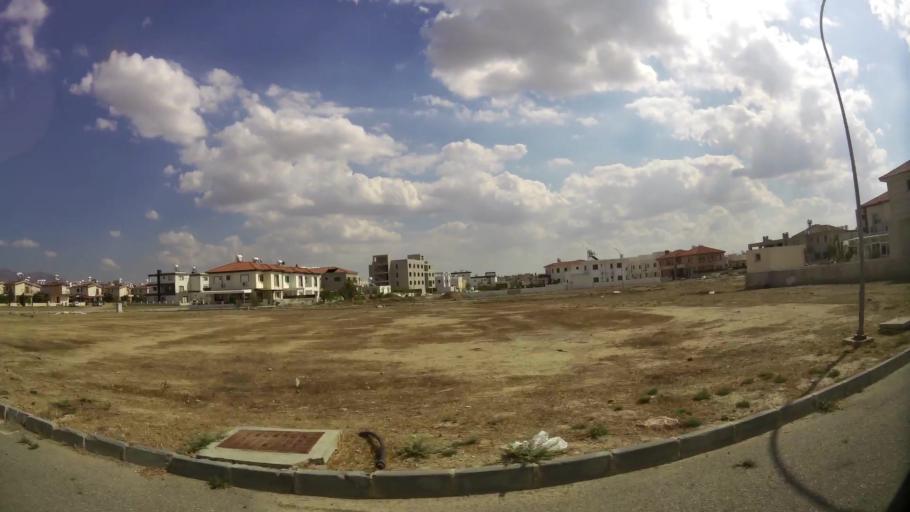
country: CY
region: Lefkosia
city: Nicosia
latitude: 35.2206
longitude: 33.2939
